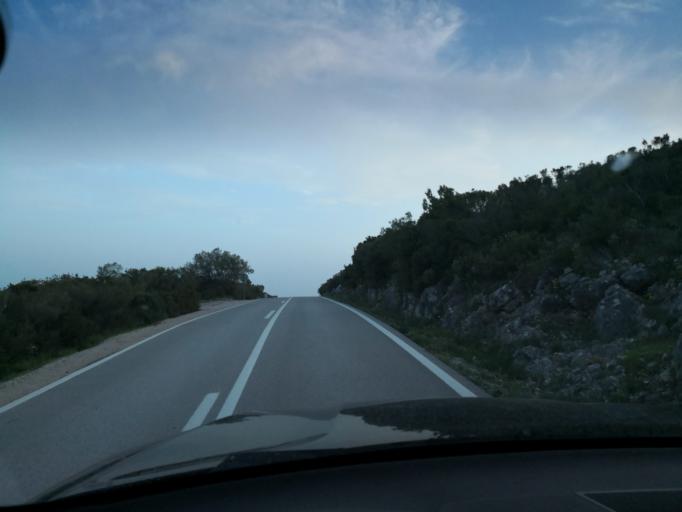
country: PT
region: Setubal
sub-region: Palmela
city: Quinta do Anjo
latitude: 38.4835
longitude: -8.9885
